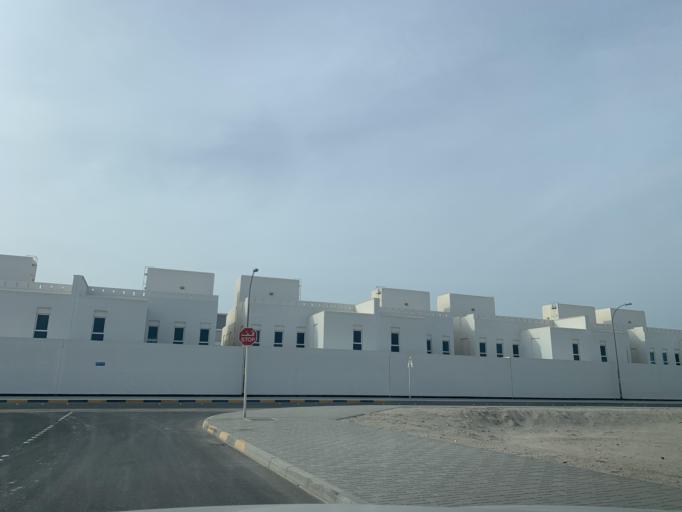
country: BH
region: Muharraq
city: Al Muharraq
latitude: 26.3164
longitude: 50.6277
